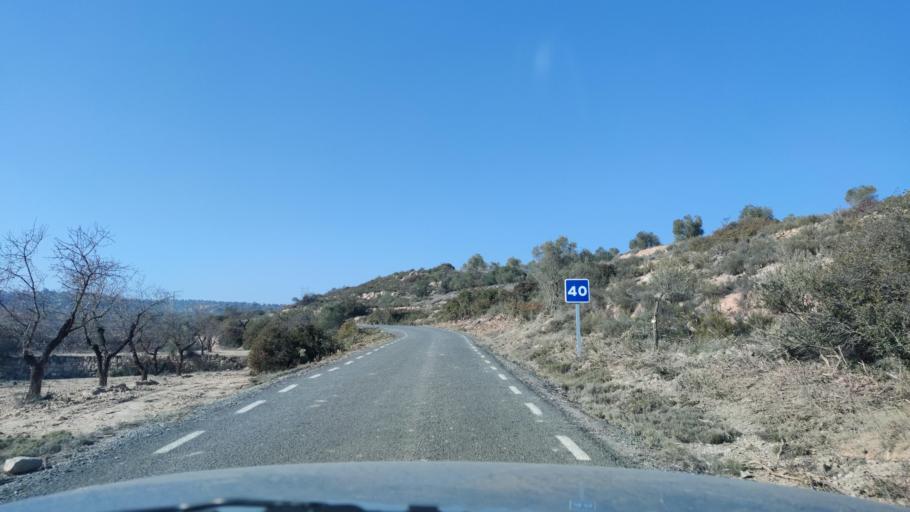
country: ES
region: Catalonia
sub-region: Provincia de Lleida
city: Torrebesses
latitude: 41.4327
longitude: 0.5768
